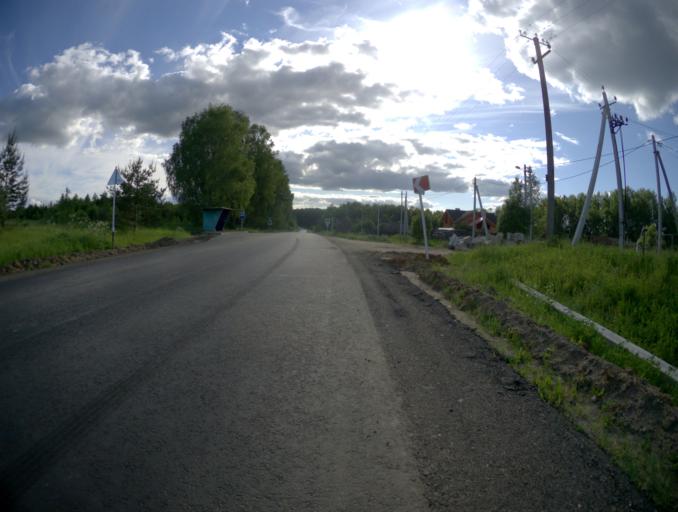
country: RU
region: Ivanovo
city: Novyye Gorki
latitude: 56.8137
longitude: 41.0667
